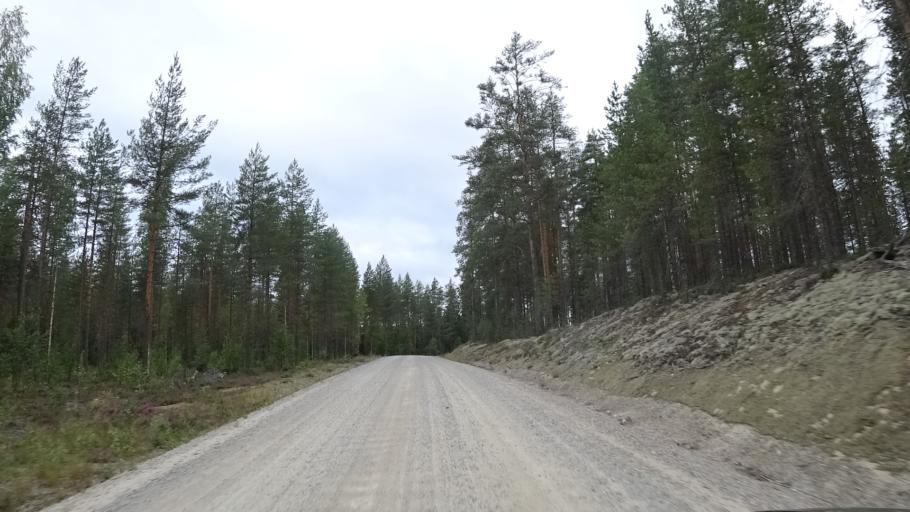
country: FI
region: North Karelia
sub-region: Pielisen Karjala
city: Lieksa
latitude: 63.2388
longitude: 30.3532
